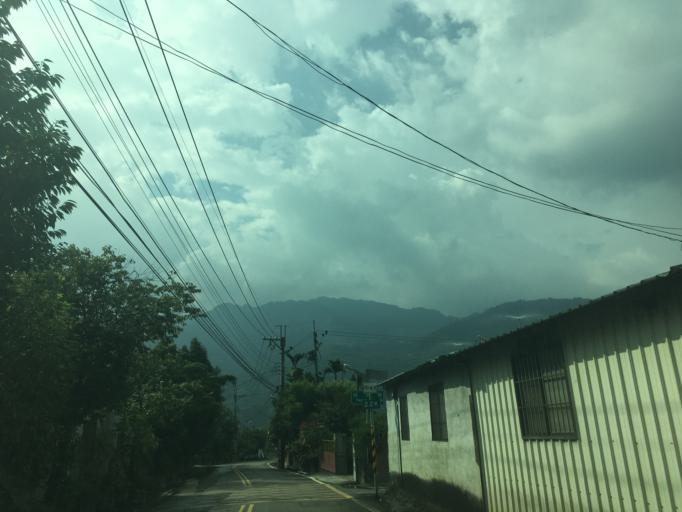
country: TW
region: Taiwan
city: Fengyuan
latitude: 24.3372
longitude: 120.9340
